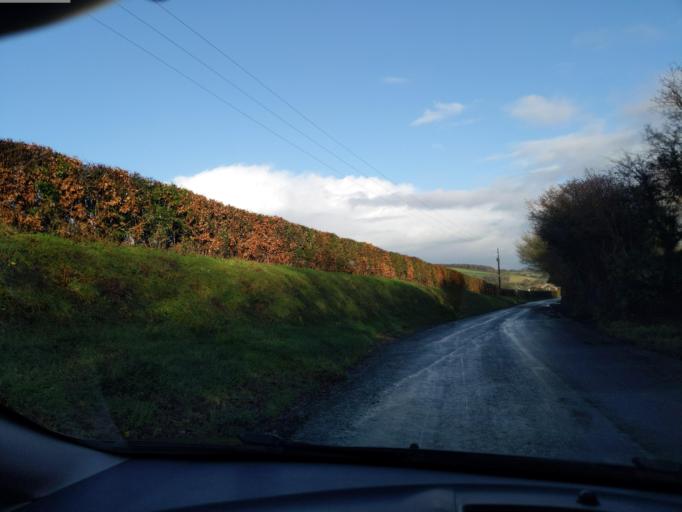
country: GB
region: England
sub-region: Devon
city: Okehampton
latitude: 50.7167
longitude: -4.0457
